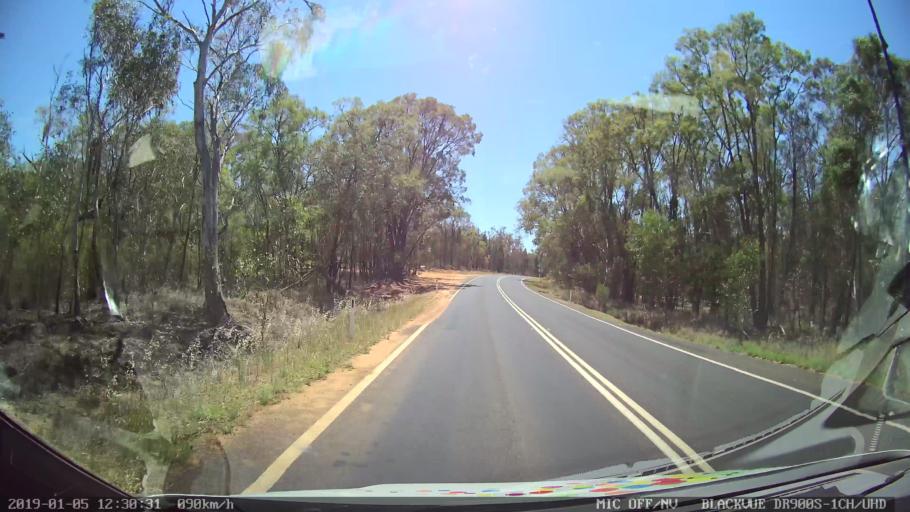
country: AU
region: New South Wales
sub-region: Warrumbungle Shire
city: Coonabarabran
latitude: -31.2270
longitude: 149.3514
